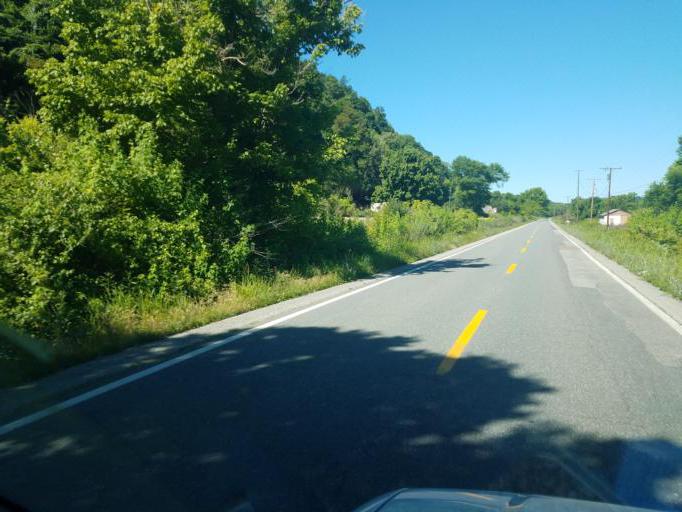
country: US
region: West Virginia
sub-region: Cabell County
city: Lesage
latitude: 38.5897
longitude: -82.1947
